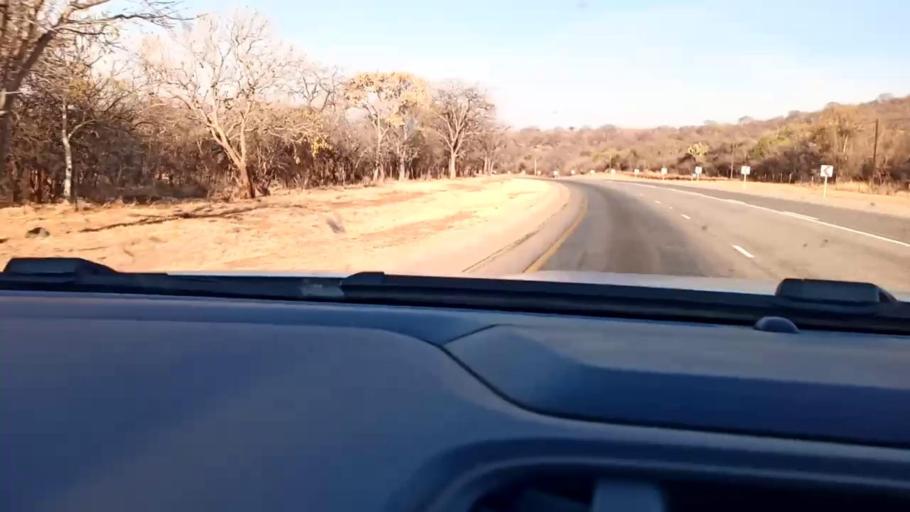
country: ZA
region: Limpopo
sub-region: Mopani District Municipality
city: Duiwelskloof
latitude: -23.6356
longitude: 30.1411
